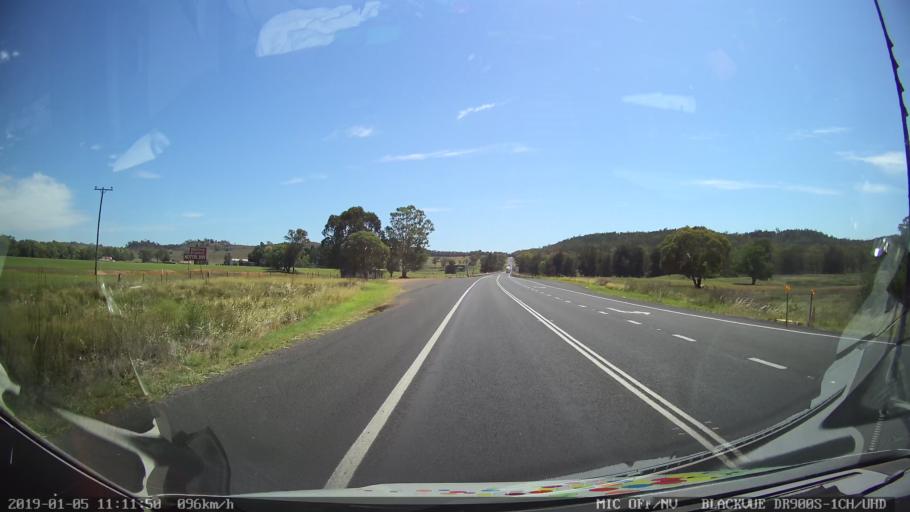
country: AU
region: New South Wales
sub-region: Warrumbungle Shire
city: Coonabarabran
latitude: -31.3884
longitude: 149.2538
